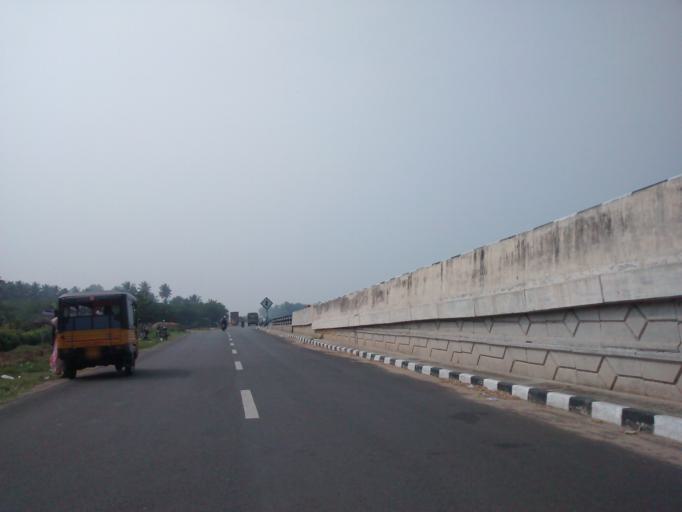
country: IN
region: Tamil Nadu
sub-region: Krishnagiri
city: Krishnagiri
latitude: 12.4804
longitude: 78.2161
